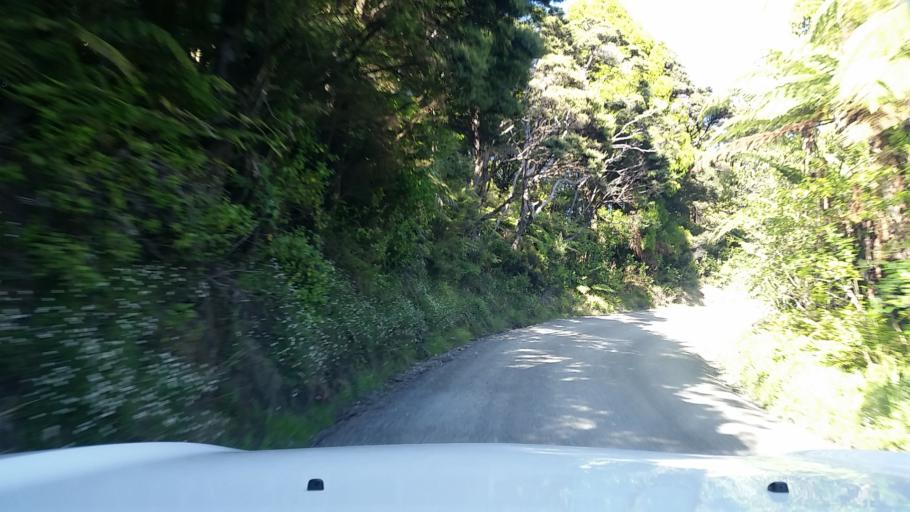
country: NZ
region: Auckland
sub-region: Auckland
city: Titirangi
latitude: -37.0217
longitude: 174.5458
